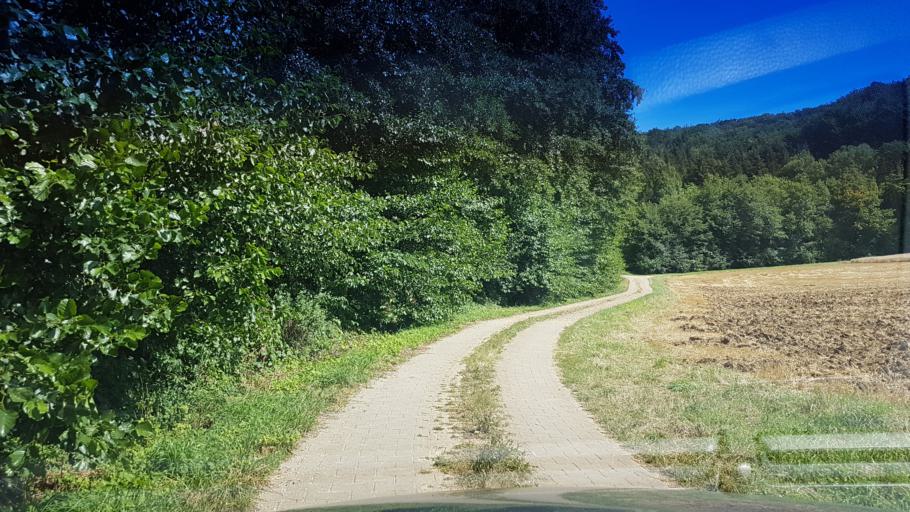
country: DE
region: Bavaria
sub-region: Upper Franconia
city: Schesslitz
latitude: 49.9434
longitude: 11.0515
